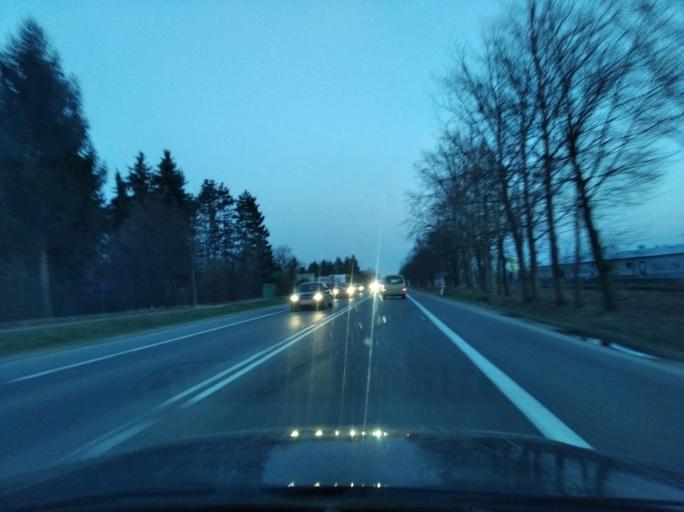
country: PL
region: Subcarpathian Voivodeship
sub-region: Powiat rzeszowski
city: Rudna Mala
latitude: 50.1043
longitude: 21.9768
